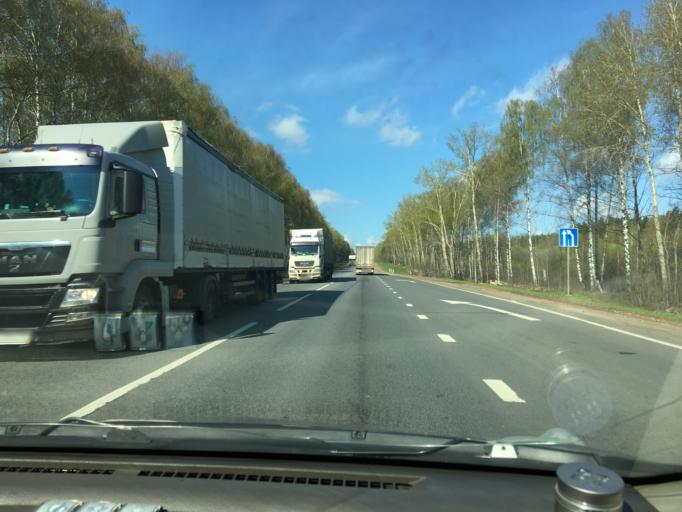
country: RU
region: Nizjnij Novgorod
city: Pamyat' Parizhskoy Kommuny
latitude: 56.0297
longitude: 44.5407
